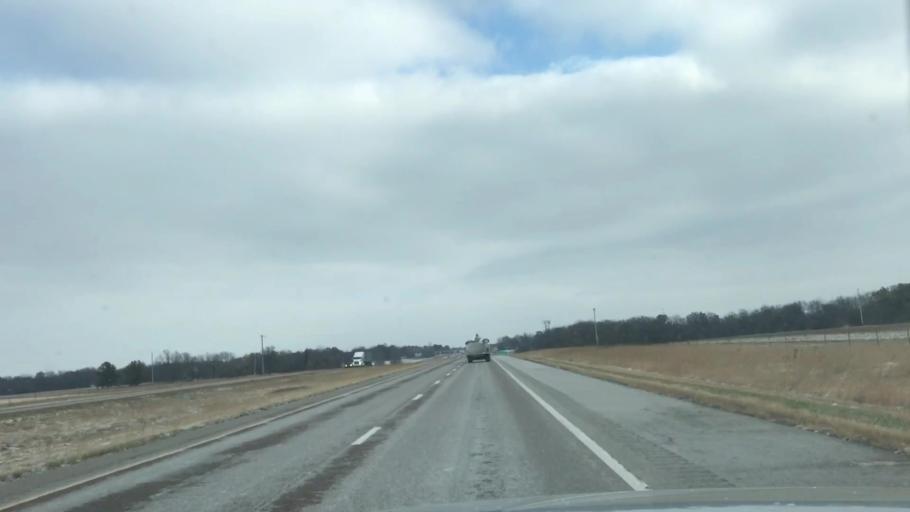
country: US
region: Illinois
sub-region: Macoupin County
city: Staunton
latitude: 38.9503
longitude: -89.7761
